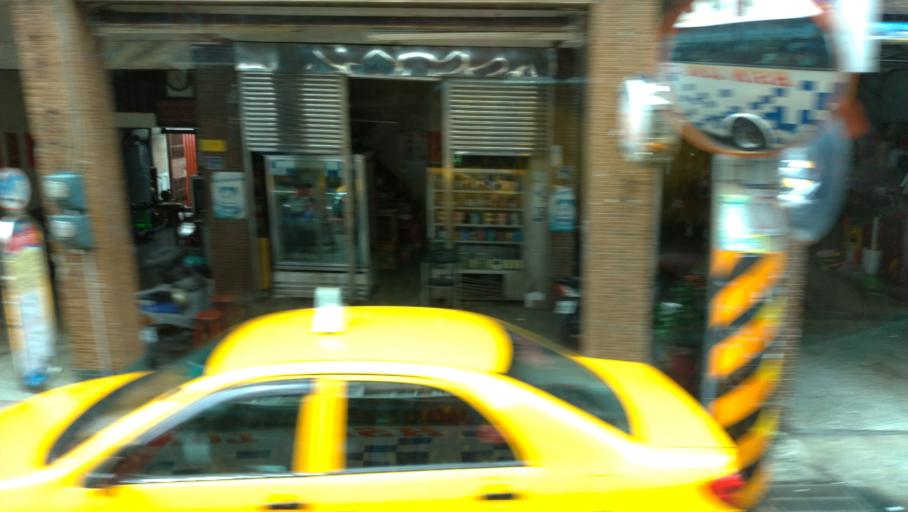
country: TW
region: Taiwan
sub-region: Keelung
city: Keelung
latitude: 25.1456
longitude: 121.7615
